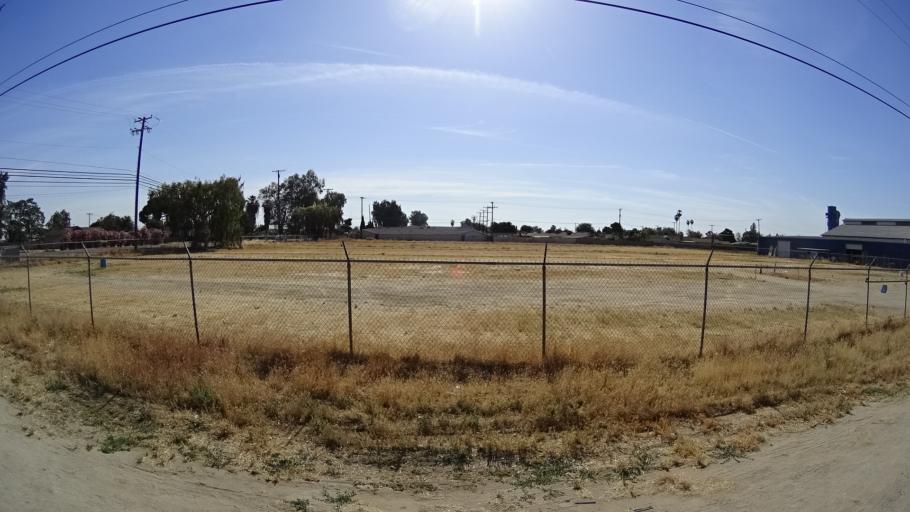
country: US
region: California
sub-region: Kings County
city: Hanford
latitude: 36.3276
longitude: -119.6168
